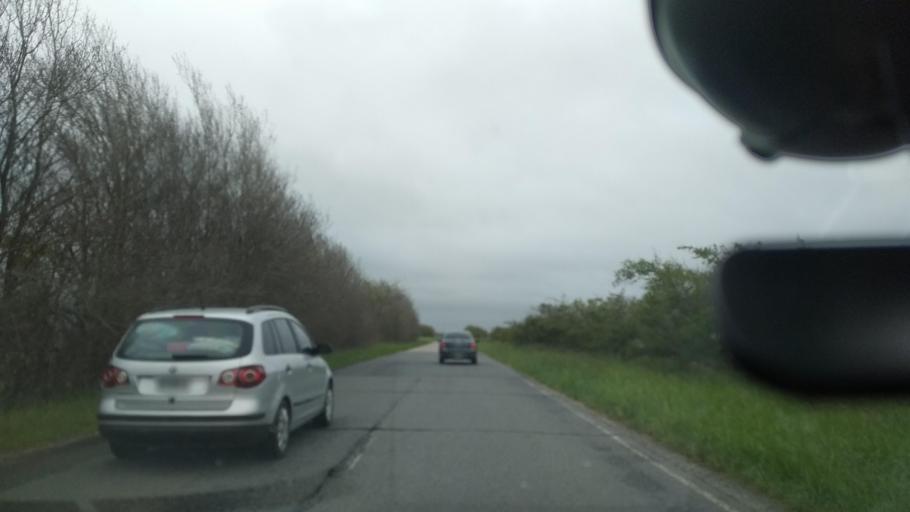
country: AR
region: Buenos Aires
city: Veronica
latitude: -35.5572
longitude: -57.3047
